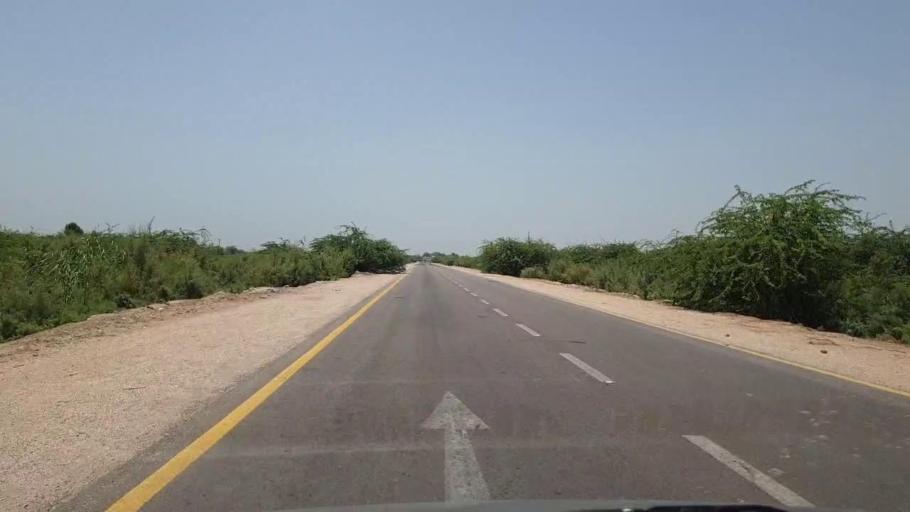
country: PK
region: Sindh
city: Sakrand
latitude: 26.1157
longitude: 68.3866
